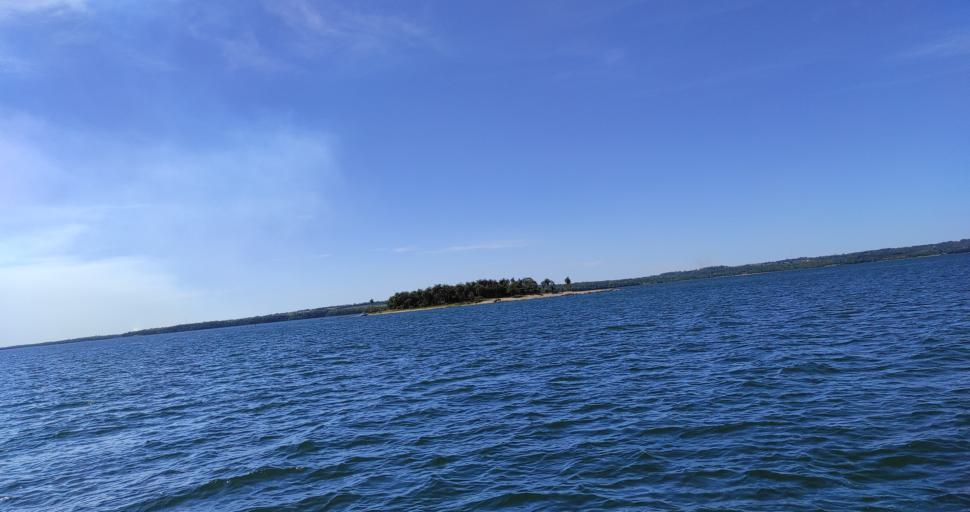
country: PY
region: Itapua
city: San Juan del Parana
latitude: -27.3435
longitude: -55.9481
